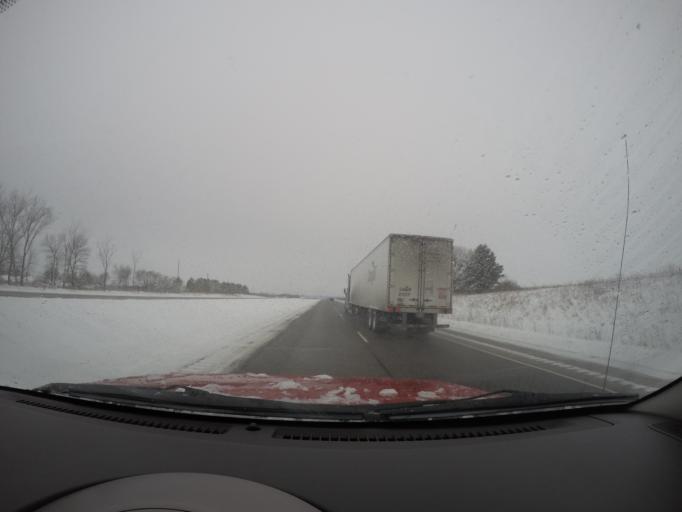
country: US
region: Minnesota
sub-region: Winona County
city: Lewiston
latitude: 43.9335
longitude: -91.8555
